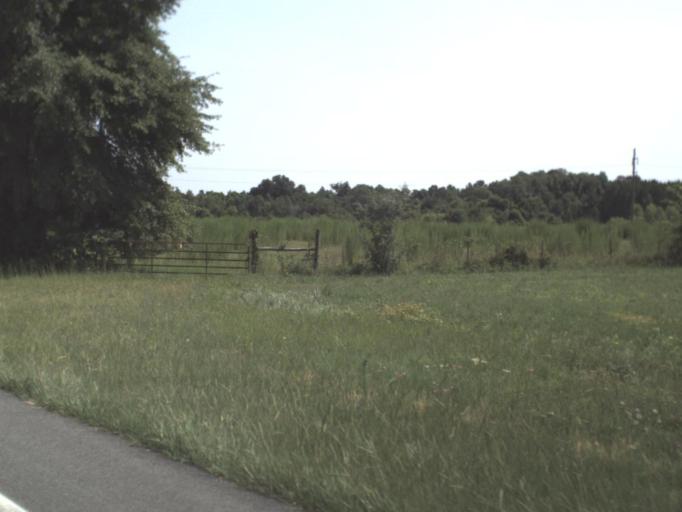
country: US
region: Florida
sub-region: Hamilton County
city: Jasper
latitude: 30.5495
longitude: -82.9787
